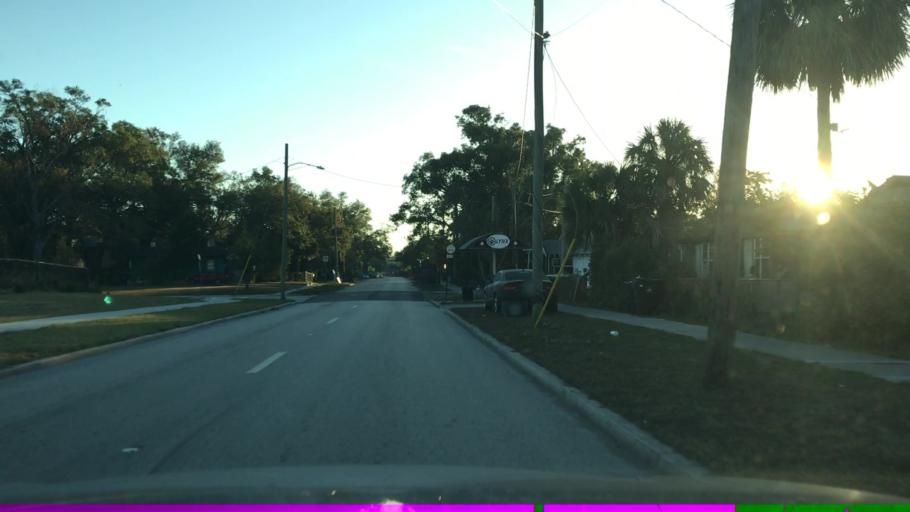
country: US
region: Florida
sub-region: Orange County
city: Orlando
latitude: 28.5366
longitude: -81.3959
